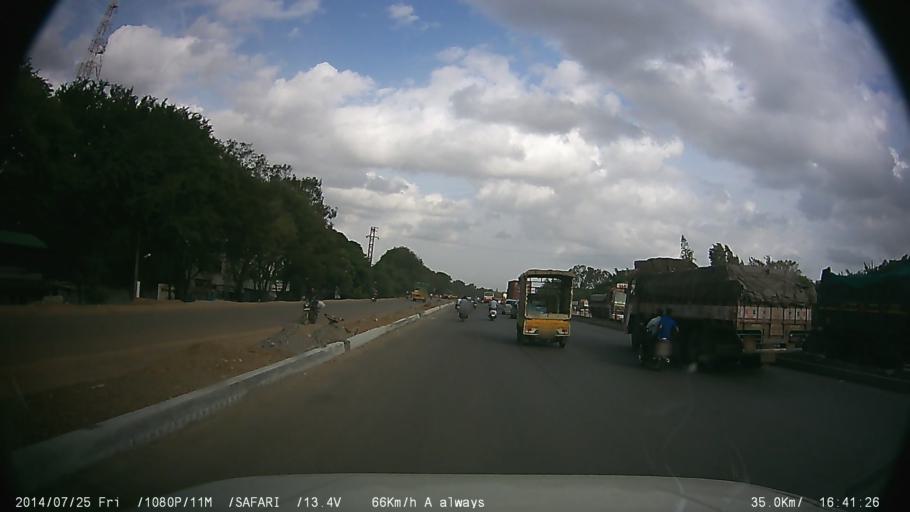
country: IN
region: Tamil Nadu
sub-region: Krishnagiri
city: Hosur
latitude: 12.7610
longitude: 77.7960
